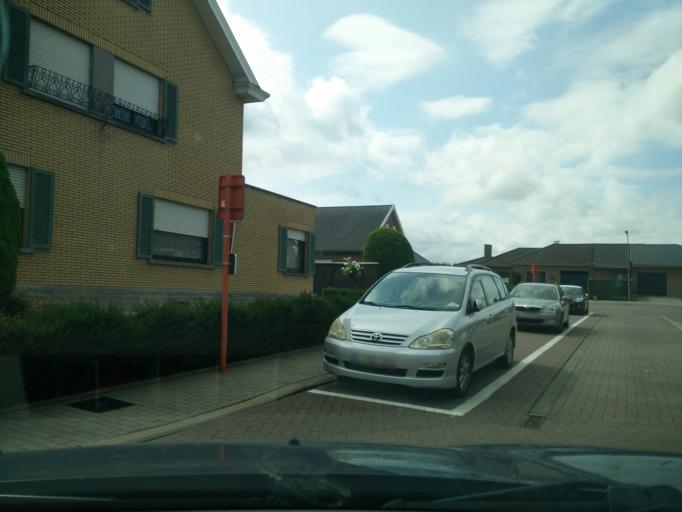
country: BE
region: Wallonia
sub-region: Province du Brabant Wallon
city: Tubize
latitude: 50.7179
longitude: 4.2060
